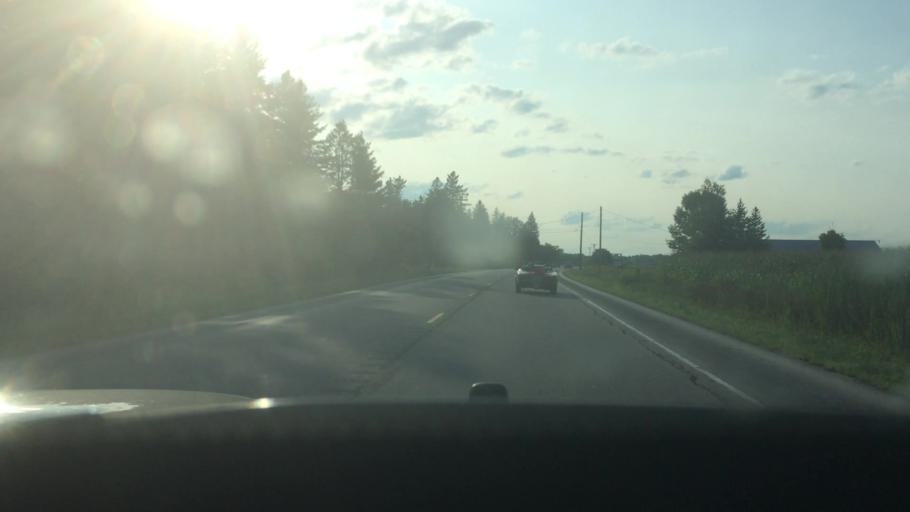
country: US
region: New York
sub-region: St. Lawrence County
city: Ogdensburg
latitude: 44.6579
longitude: -75.3251
